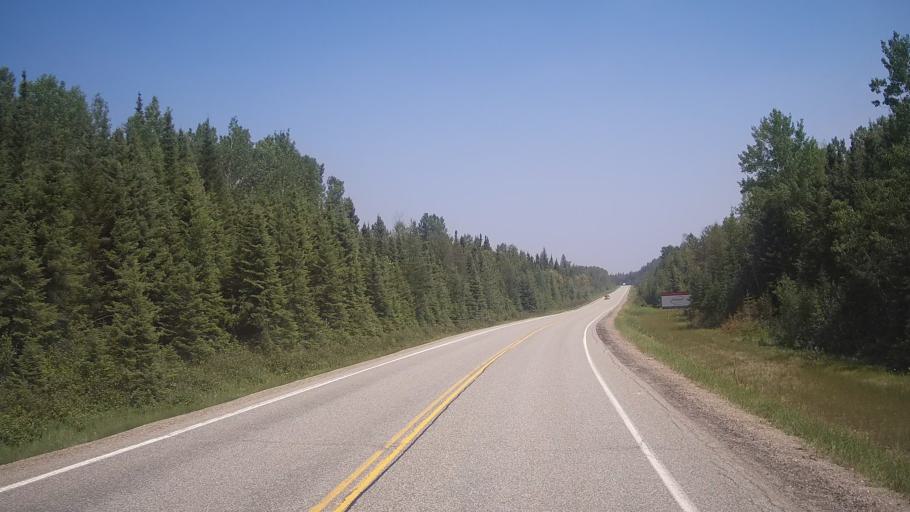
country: CA
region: Ontario
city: Timmins
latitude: 48.2346
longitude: -81.5760
